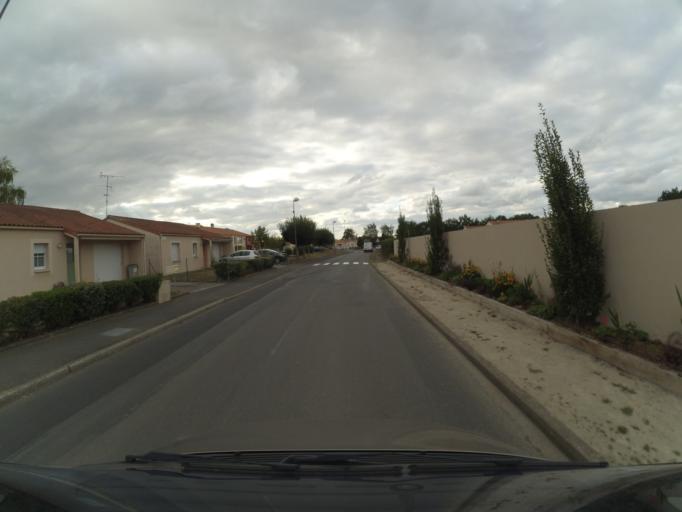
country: FR
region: Pays de la Loire
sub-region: Departement de la Vendee
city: Saint-Andre-Treize-Voies
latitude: 46.9110
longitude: -1.3800
